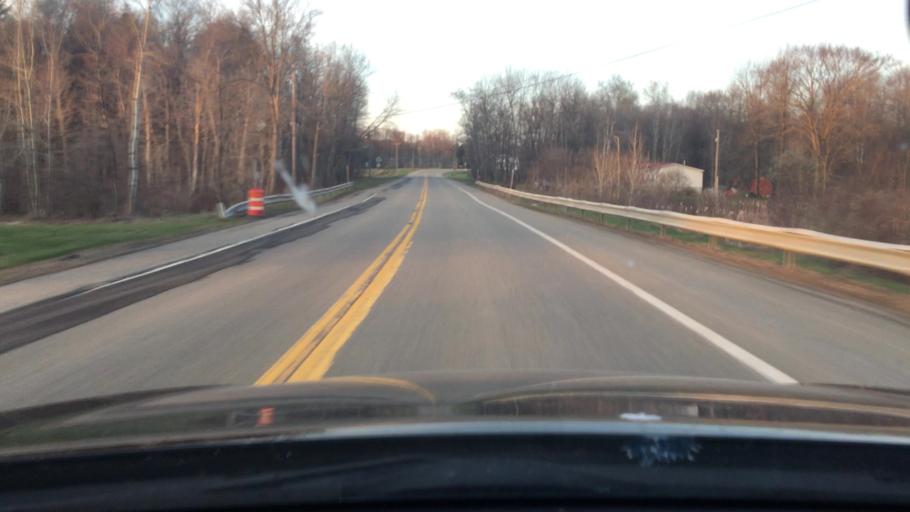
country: US
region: New York
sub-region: Cattaraugus County
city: Randolph
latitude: 42.1912
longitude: -78.9148
